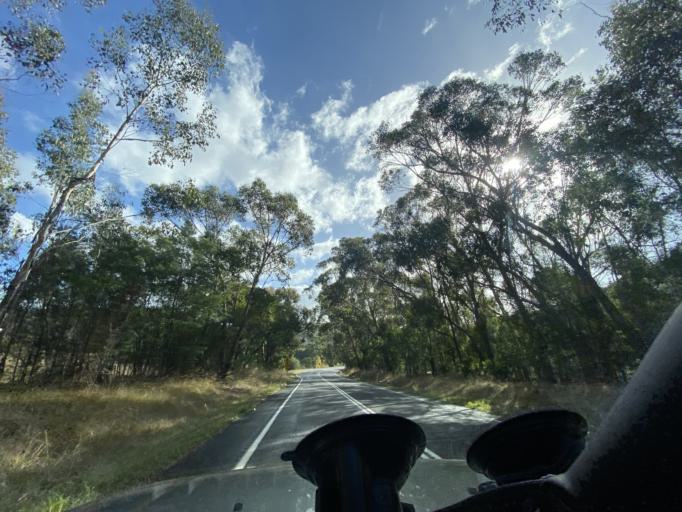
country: AU
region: Victoria
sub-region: Murrindindi
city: Kinglake West
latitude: -37.3354
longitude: 145.3424
